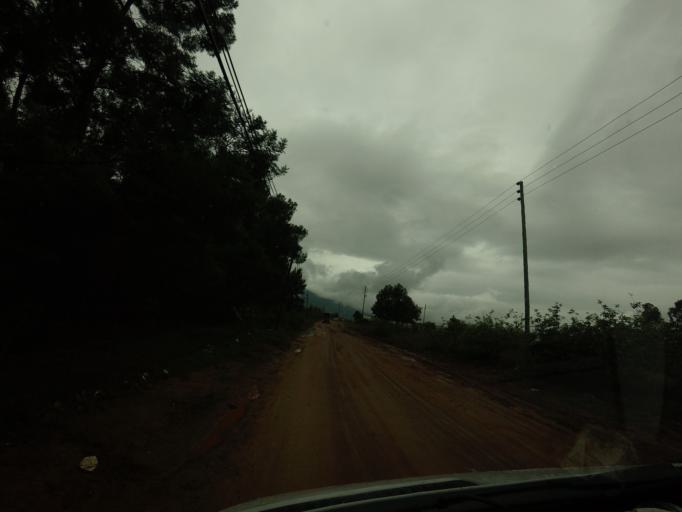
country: SZ
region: Hhohho
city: Lobamba
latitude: -26.4721
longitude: 31.2041
